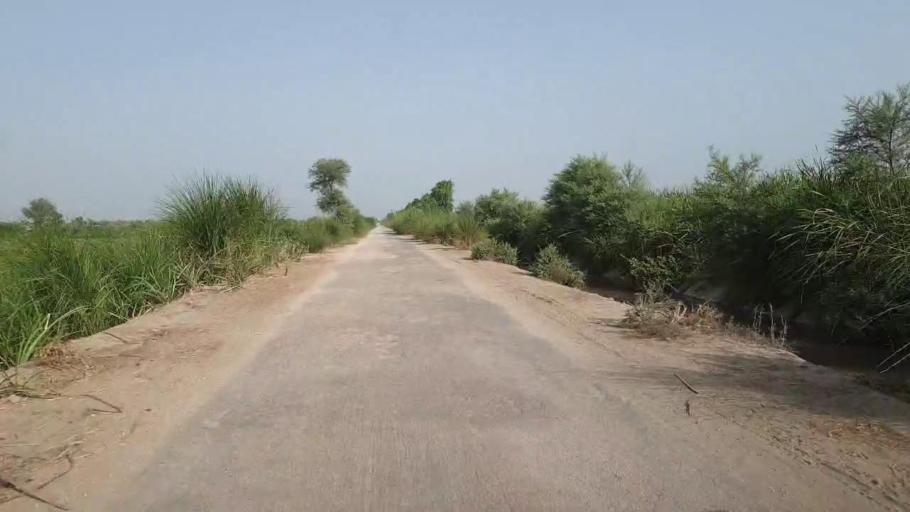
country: PK
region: Sindh
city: Daur
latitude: 26.3465
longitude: 68.1771
